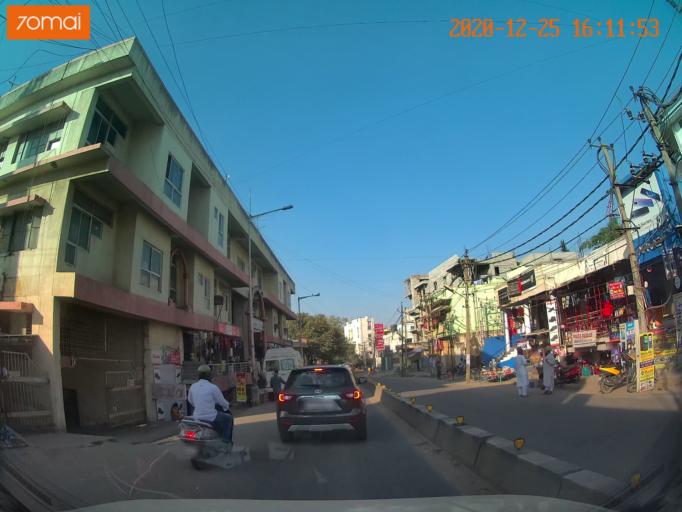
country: IN
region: Karnataka
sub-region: Bangalore Urban
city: Bangalore
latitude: 12.9056
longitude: 77.6276
